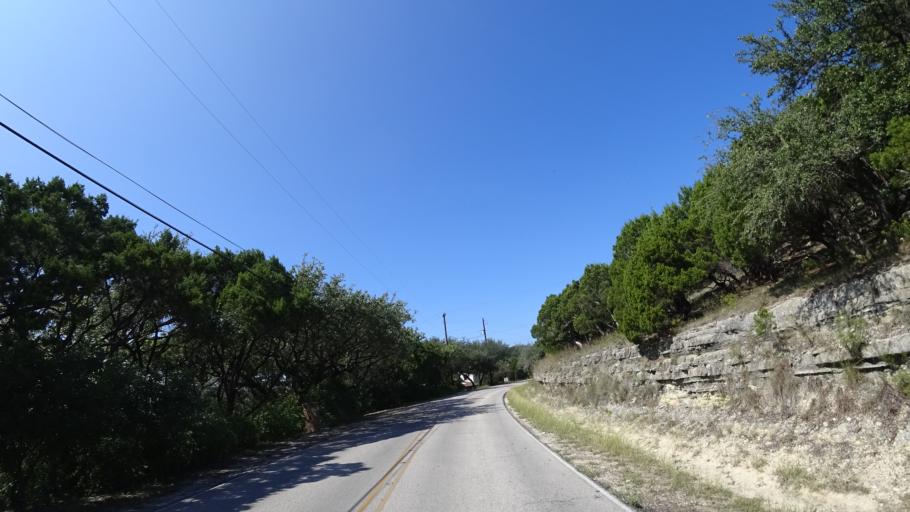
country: US
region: Texas
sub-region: Travis County
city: West Lake Hills
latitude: 30.2940
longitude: -97.8009
